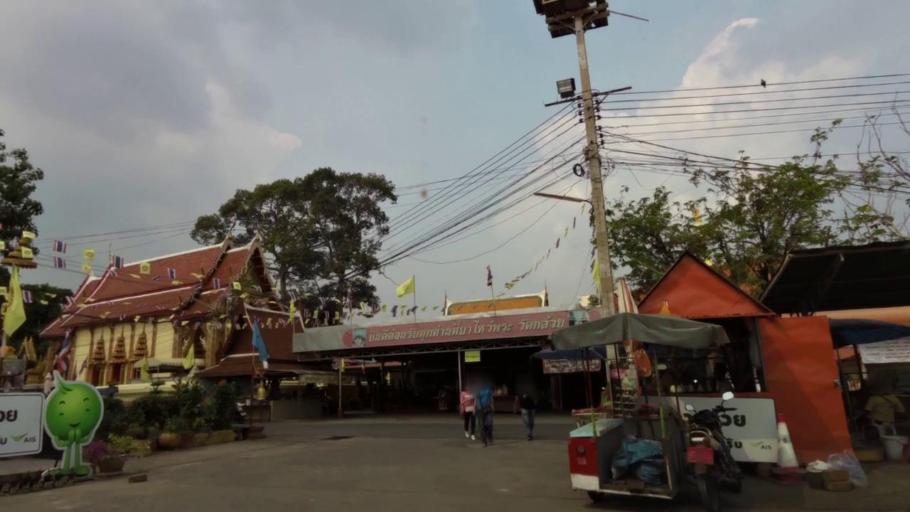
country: TH
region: Phra Nakhon Si Ayutthaya
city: Phra Nakhon Si Ayutthaya
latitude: 14.3367
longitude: 100.5808
